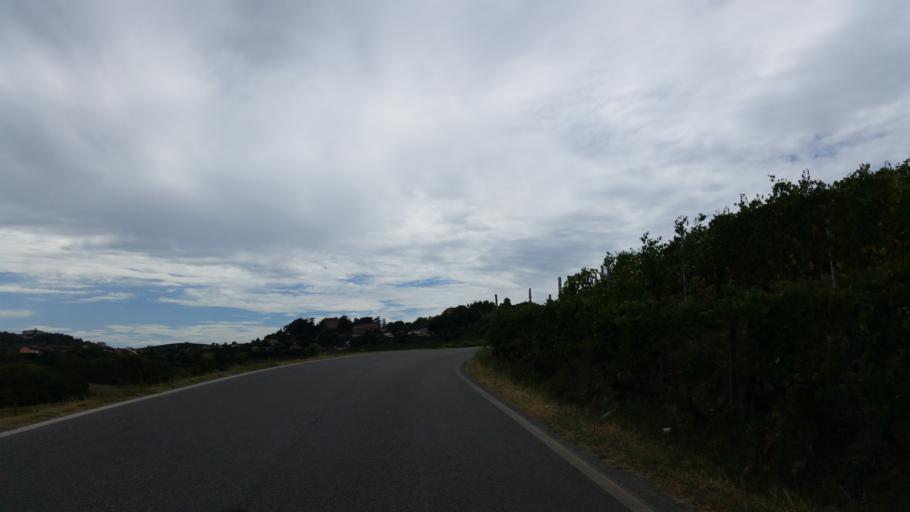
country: IT
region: Piedmont
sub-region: Provincia di Asti
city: San Martino Alfieri
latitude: 44.8221
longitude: 8.1247
